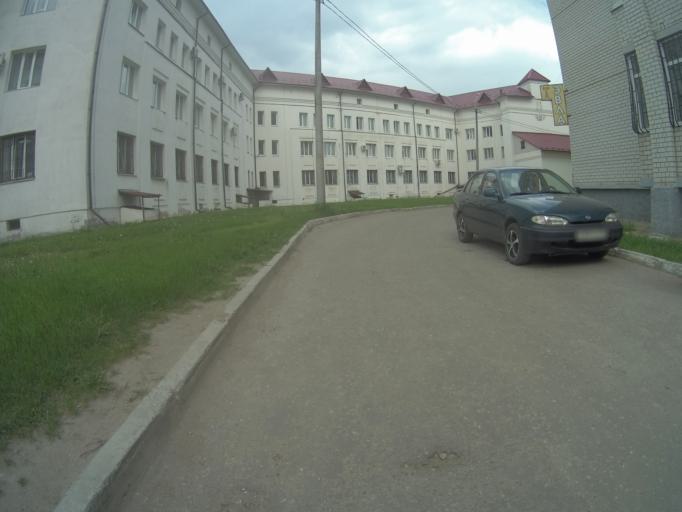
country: RU
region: Vladimir
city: Kommunar
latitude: 56.1643
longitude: 40.4661
